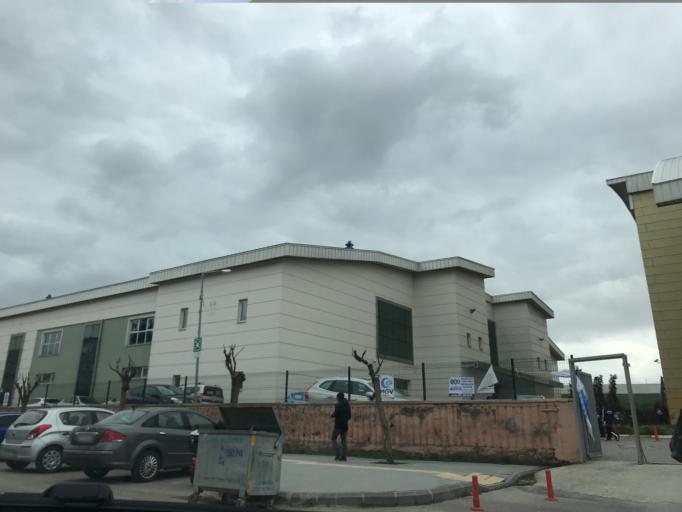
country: TR
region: Yalova
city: Yalova
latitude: 40.6543
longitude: 29.2605
